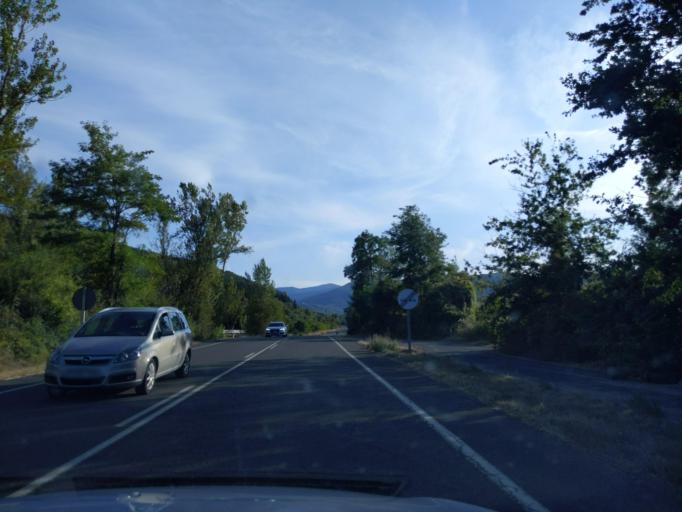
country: ES
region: La Rioja
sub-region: Provincia de La Rioja
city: Ojacastro
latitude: 42.3595
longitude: -2.9890
